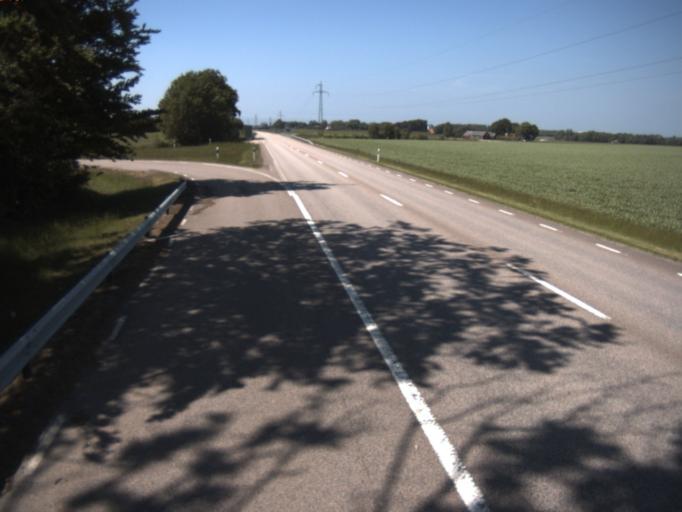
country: SE
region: Skane
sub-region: Helsingborg
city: Barslov
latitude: 56.0138
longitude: 12.8114
